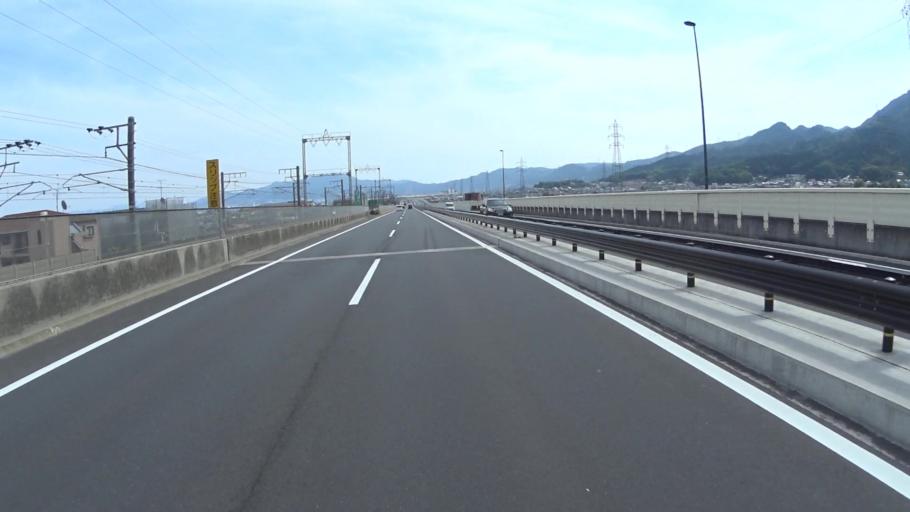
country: JP
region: Shiga Prefecture
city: Otsu-shi
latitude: 35.0694
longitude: 135.8776
